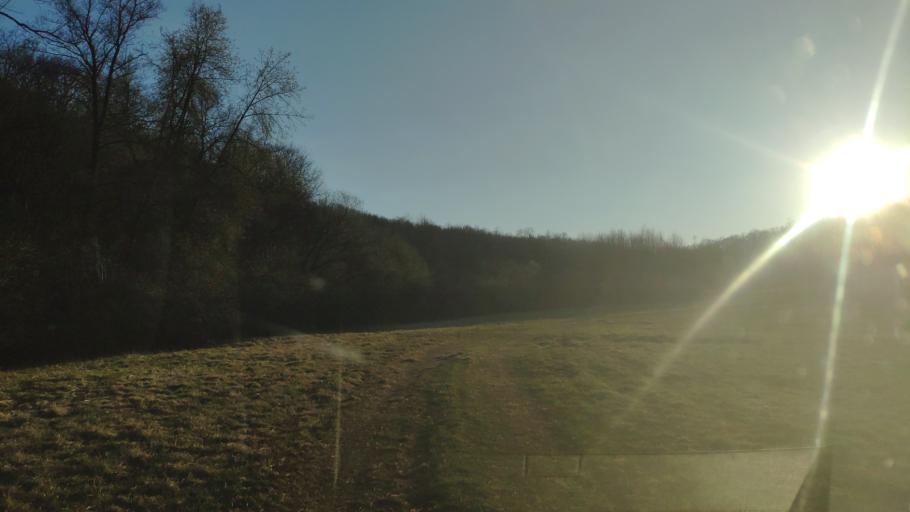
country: SK
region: Banskobystricky
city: Revuca
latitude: 48.5211
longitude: 20.3092
